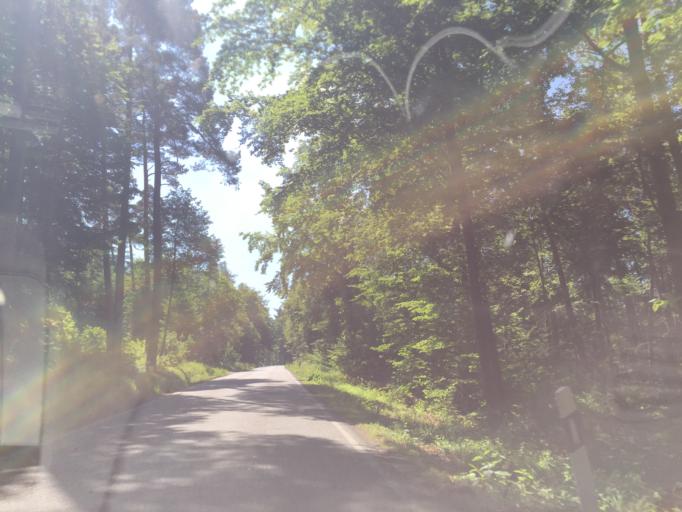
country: DE
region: Baden-Wuerttemberg
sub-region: Karlsruhe Region
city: Walldurn
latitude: 49.6192
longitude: 9.3293
